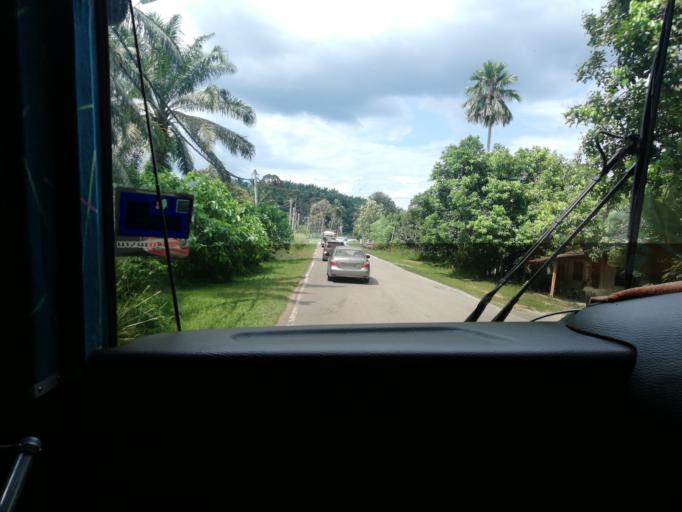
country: MY
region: Perak
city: Parit Buntar
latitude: 5.1870
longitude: 100.6030
